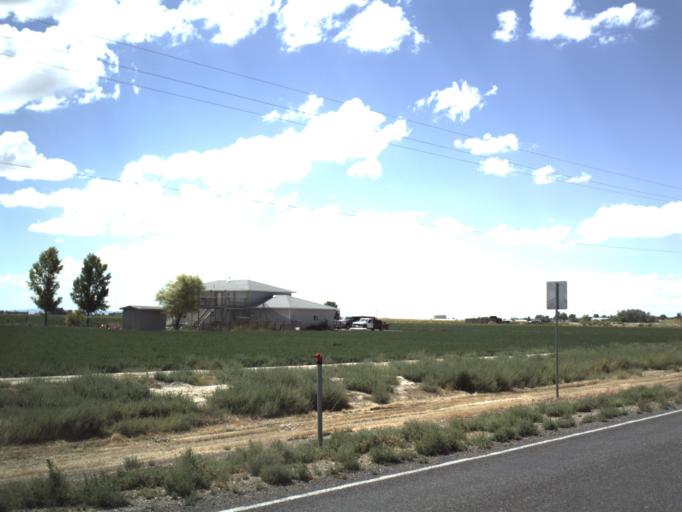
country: US
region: Utah
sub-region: Millard County
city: Delta
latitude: 39.3529
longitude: -112.5379
